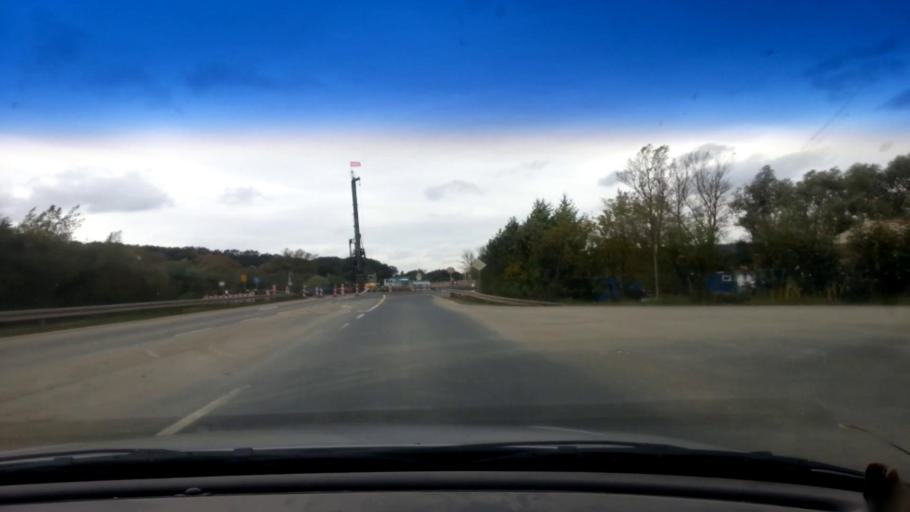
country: DE
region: Bavaria
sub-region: Upper Franconia
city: Baunach
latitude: 49.9757
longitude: 10.8616
